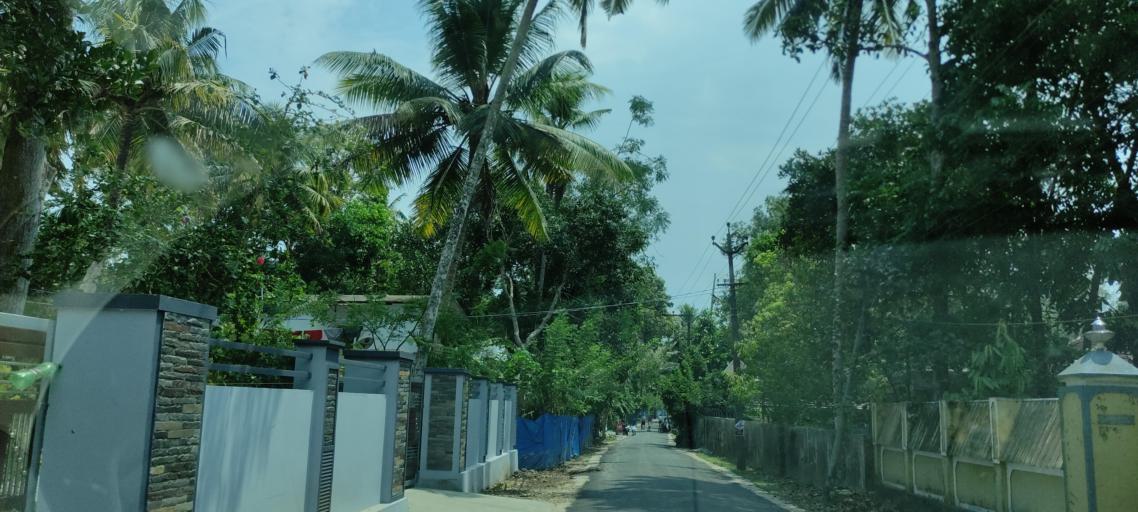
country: IN
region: Kerala
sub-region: Alappuzha
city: Vayalar
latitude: 9.7216
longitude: 76.3407
